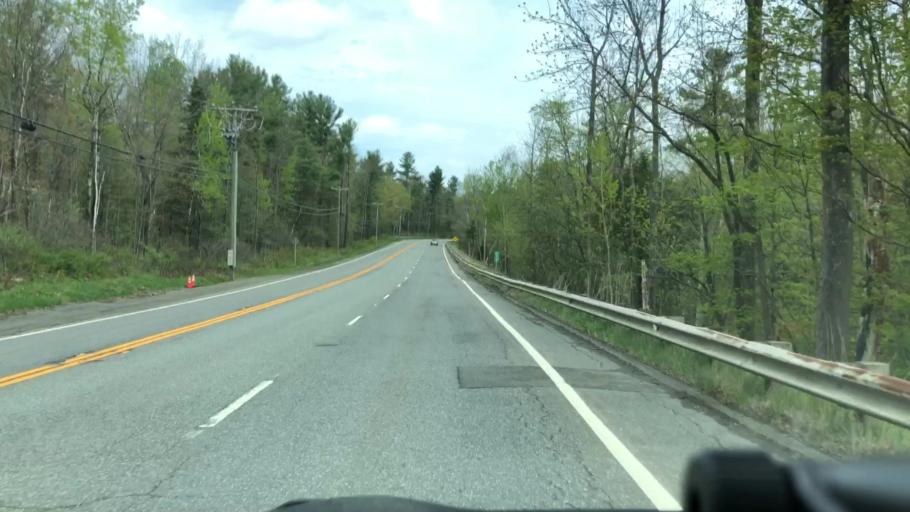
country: US
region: Massachusetts
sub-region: Berkshire County
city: Hinsdale
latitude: 42.4980
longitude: -73.1032
